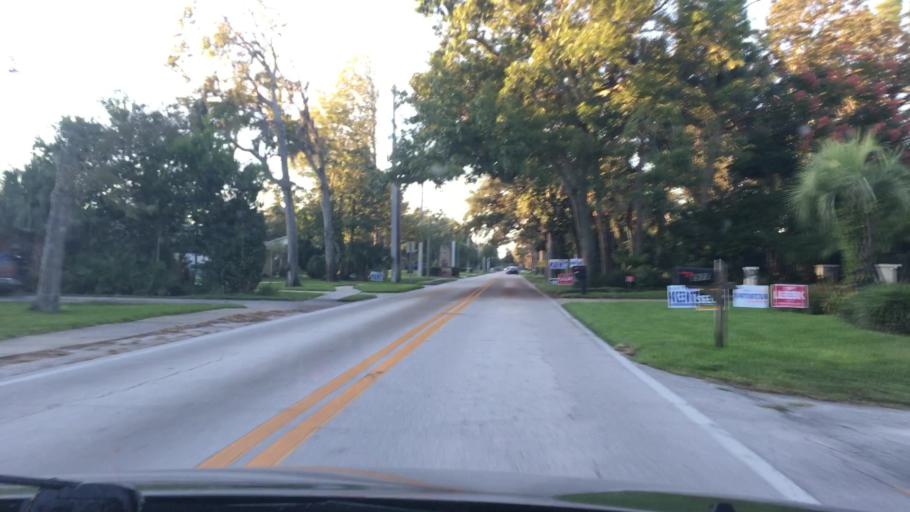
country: US
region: Florida
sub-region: Volusia County
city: Ormond Beach
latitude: 29.3011
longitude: -81.0630
